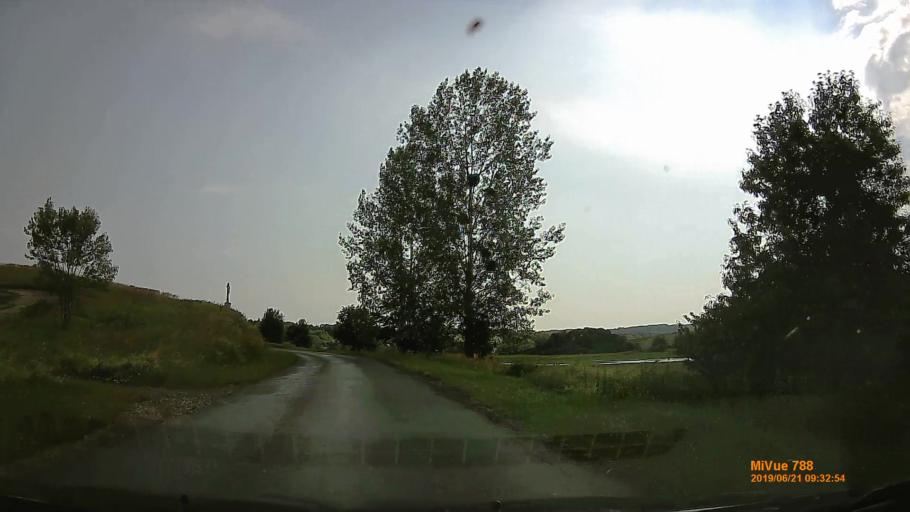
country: HU
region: Somogy
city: Taszar
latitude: 46.3150
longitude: 17.8860
